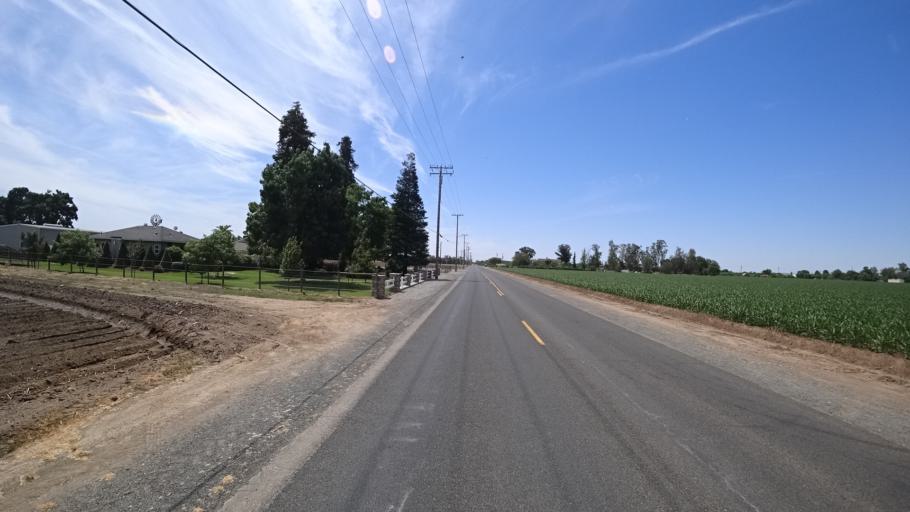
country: US
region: California
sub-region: Kings County
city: Armona
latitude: 36.3467
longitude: -119.6910
